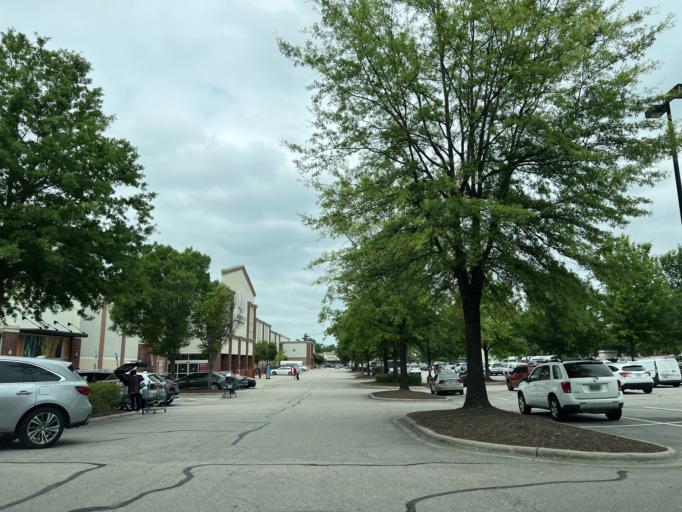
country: US
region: North Carolina
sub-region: Wake County
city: Raleigh
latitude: 35.8727
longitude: -78.5844
